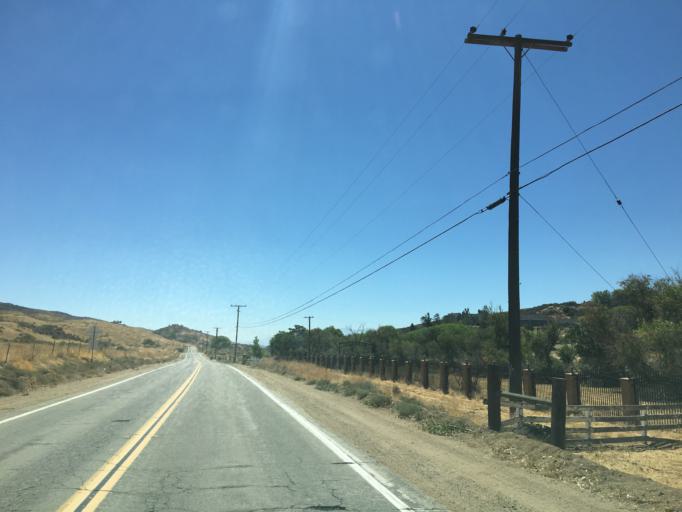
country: US
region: California
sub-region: Los Angeles County
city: Leona Valley
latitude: 34.6284
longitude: -118.3194
